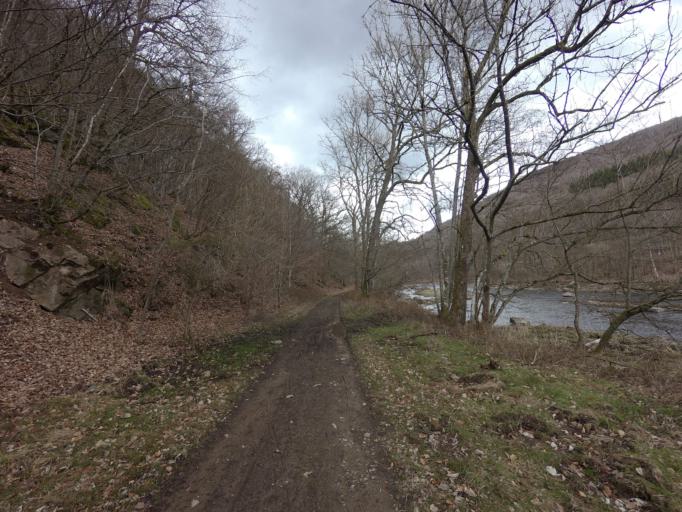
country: BE
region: Wallonia
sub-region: Province de Liege
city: Aywaille
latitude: 50.4330
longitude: 5.7321
